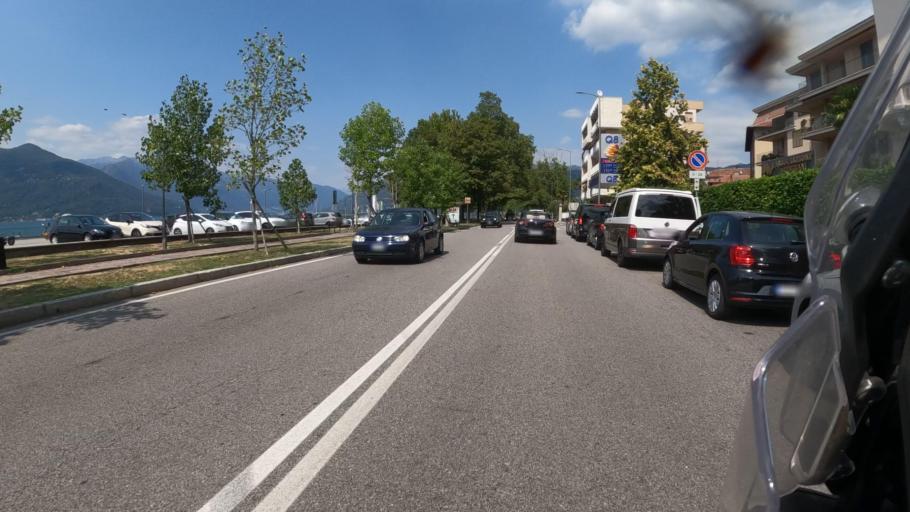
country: IT
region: Lombardy
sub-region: Provincia di Varese
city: Luino
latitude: 45.9978
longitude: 8.7345
